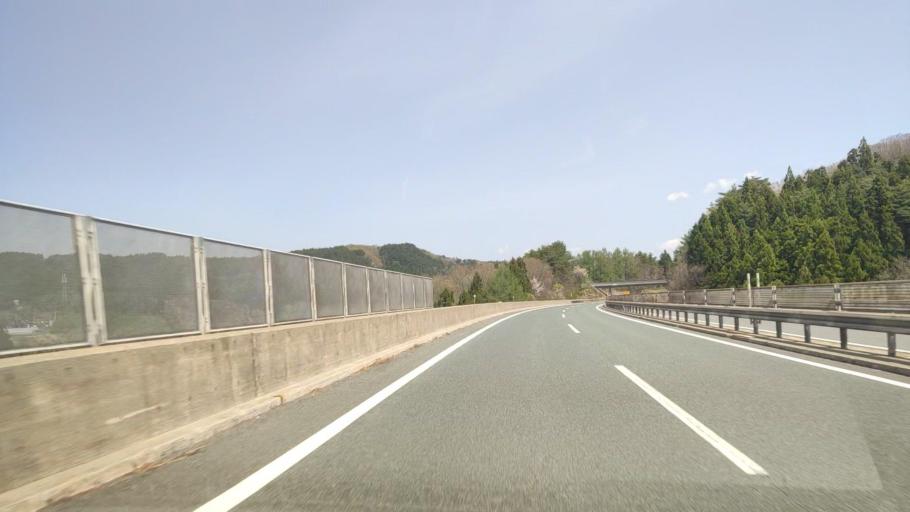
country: JP
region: Iwate
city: Ichinohe
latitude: 40.1697
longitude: 141.1389
